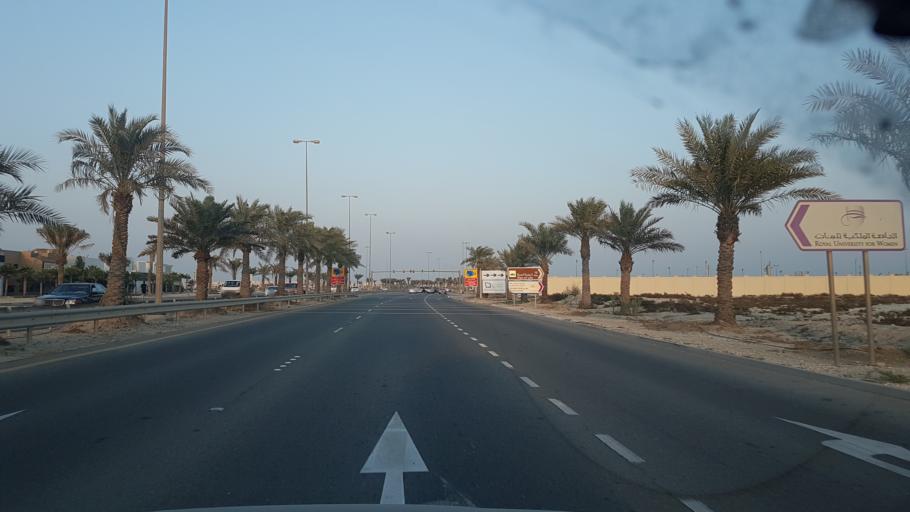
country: BH
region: Northern
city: Ar Rifa'
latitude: 26.1003
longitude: 50.5518
